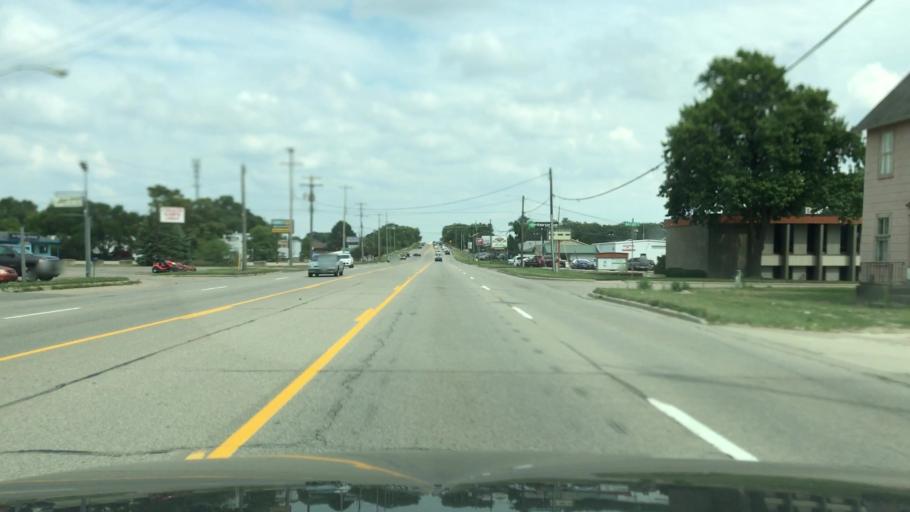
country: US
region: Michigan
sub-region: Kent County
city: Grandville
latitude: 42.9136
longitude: -85.7589
